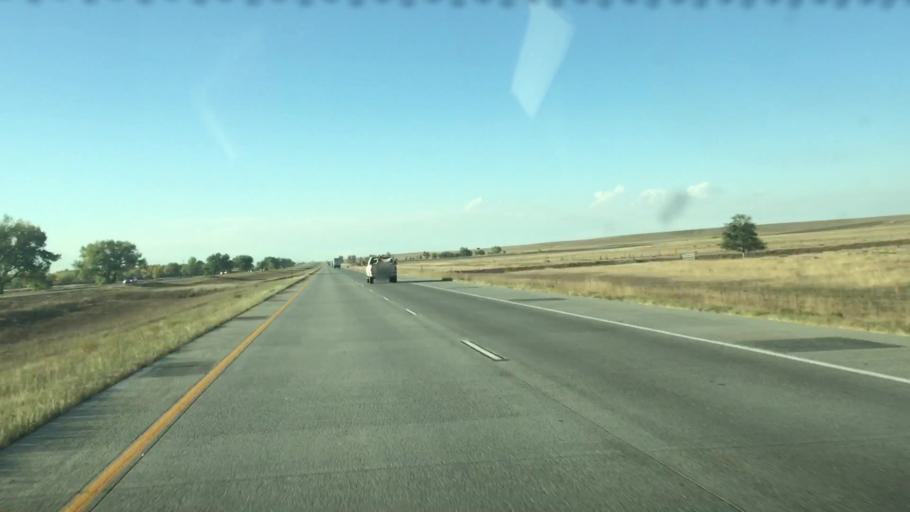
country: US
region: Colorado
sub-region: Arapahoe County
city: Byers
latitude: 39.5579
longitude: -104.0082
